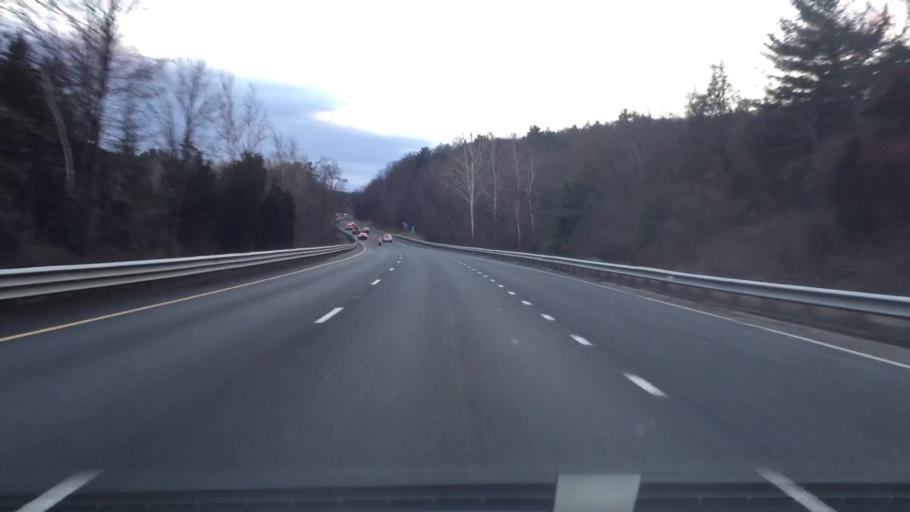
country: US
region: Massachusetts
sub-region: Hampshire County
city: South Hadley
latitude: 42.2523
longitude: -72.6225
